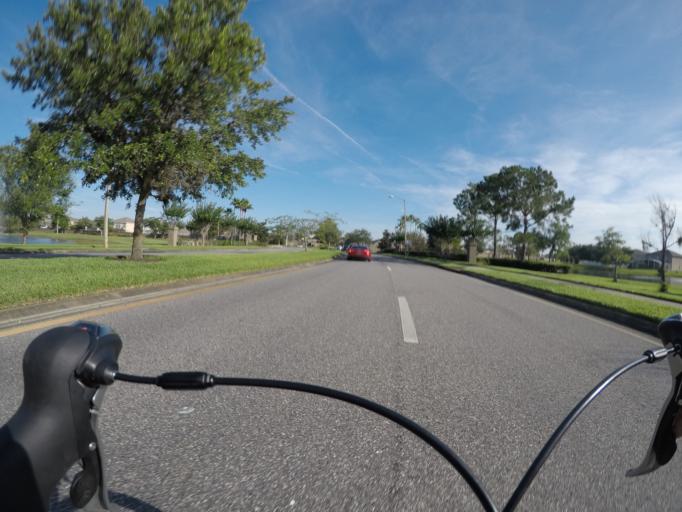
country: US
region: Florida
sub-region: Osceola County
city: Buenaventura Lakes
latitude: 28.3603
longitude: -81.3491
